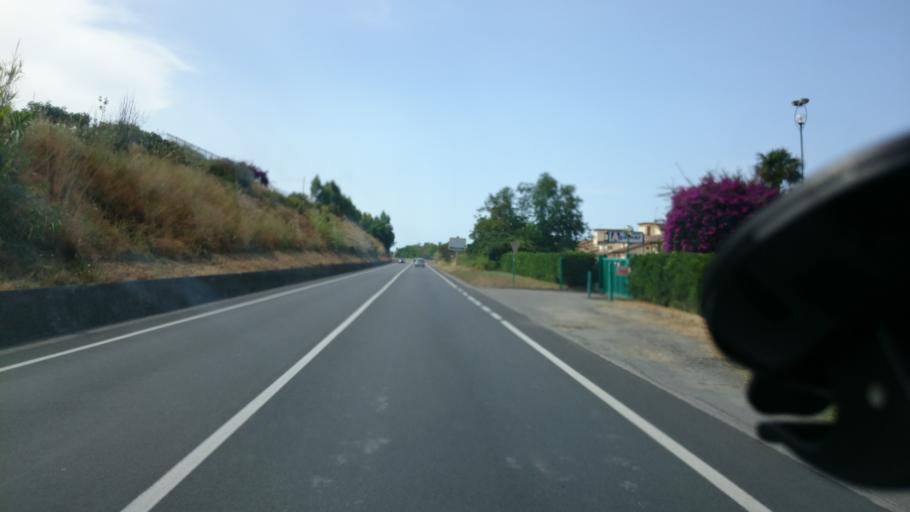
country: IT
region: Calabria
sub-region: Provincia di Cosenza
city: Diamante
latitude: 39.7037
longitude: 15.8141
